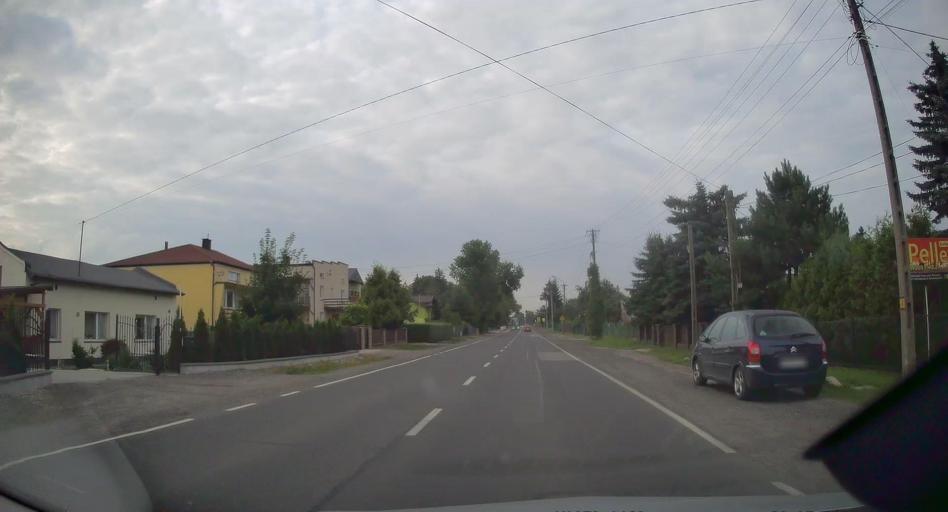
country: PL
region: Lodz Voivodeship
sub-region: Powiat radomszczanski
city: Radomsko
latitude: 51.0951
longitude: 19.4590
